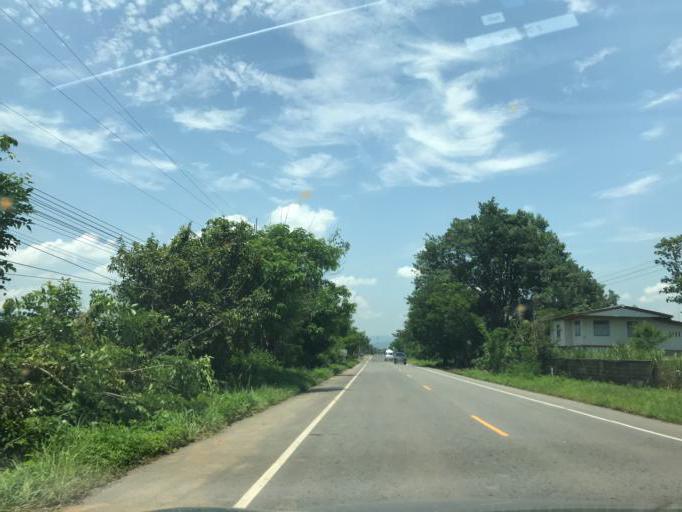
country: TH
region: Phayao
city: Phu Sang
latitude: 19.5840
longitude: 100.3075
